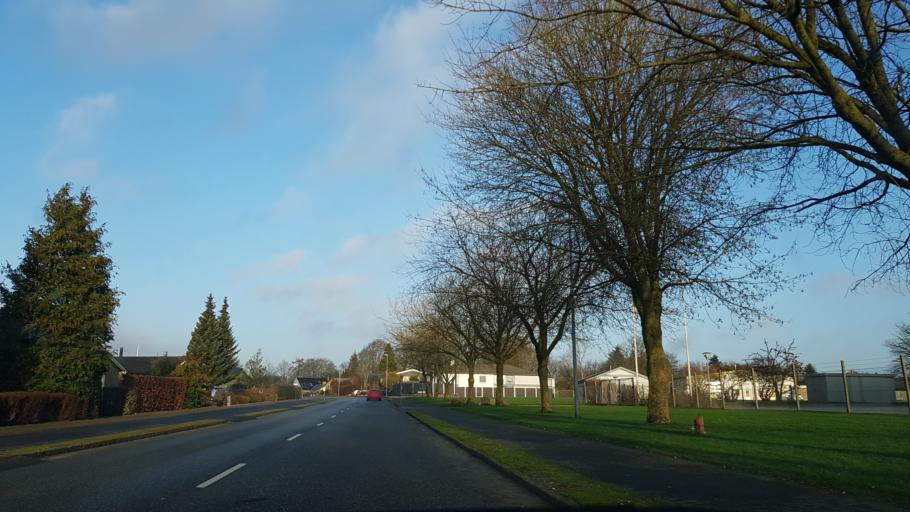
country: DK
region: South Denmark
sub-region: Haderslev Kommune
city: Haderslev
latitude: 55.2359
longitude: 9.4981
